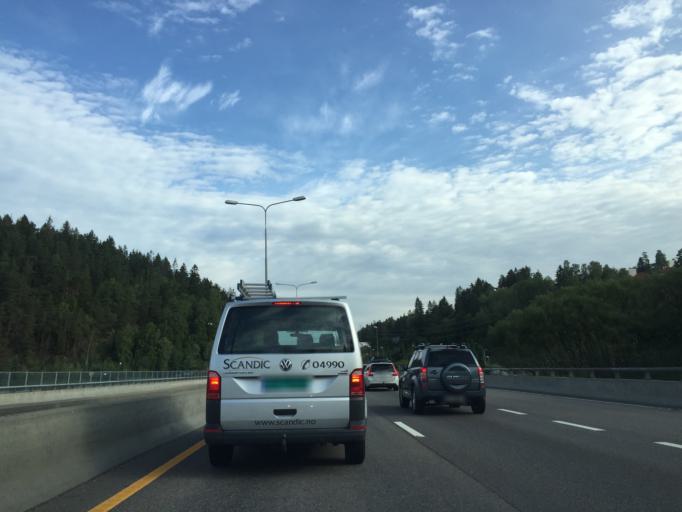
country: NO
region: Akershus
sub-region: Oppegard
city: Kolbotn
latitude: 59.8615
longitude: 10.8308
